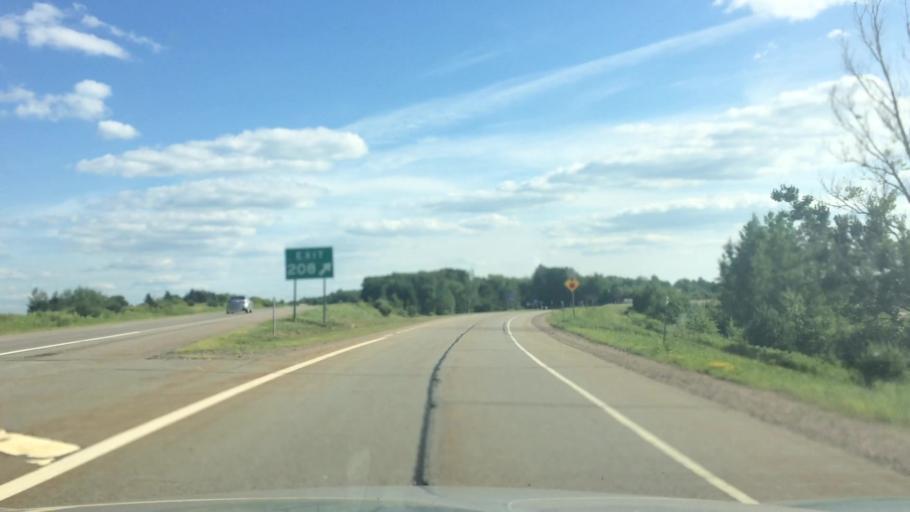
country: US
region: Wisconsin
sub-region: Lincoln County
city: Merrill
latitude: 45.1817
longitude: -89.6469
